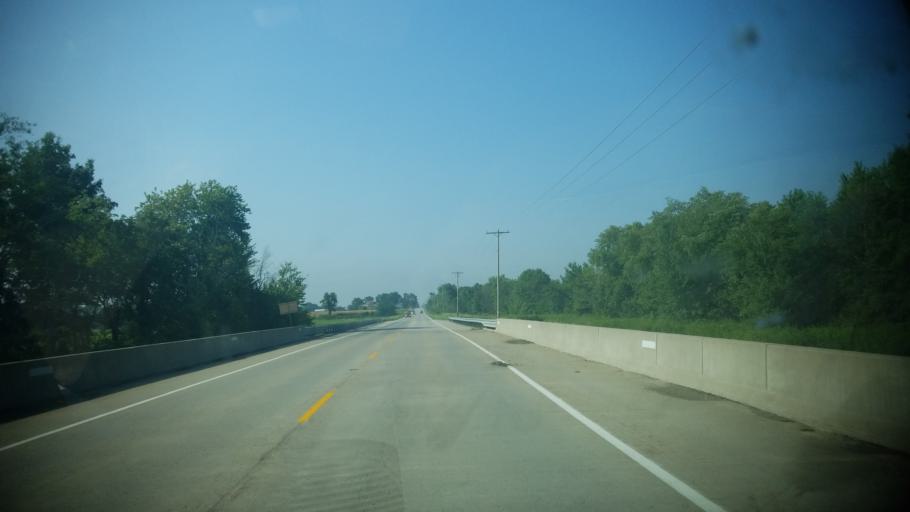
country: US
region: Illinois
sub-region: Clay County
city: Flora
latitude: 38.5961
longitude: -88.4386
